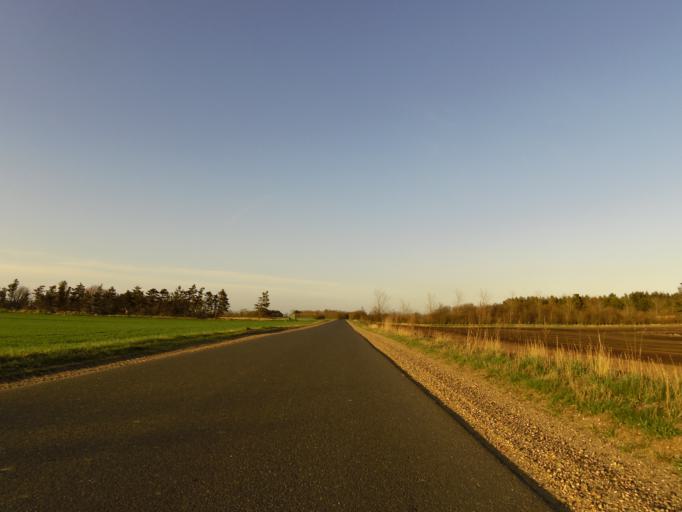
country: DK
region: Central Jutland
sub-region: Holstebro Kommune
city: Vinderup
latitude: 56.5132
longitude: 8.7648
